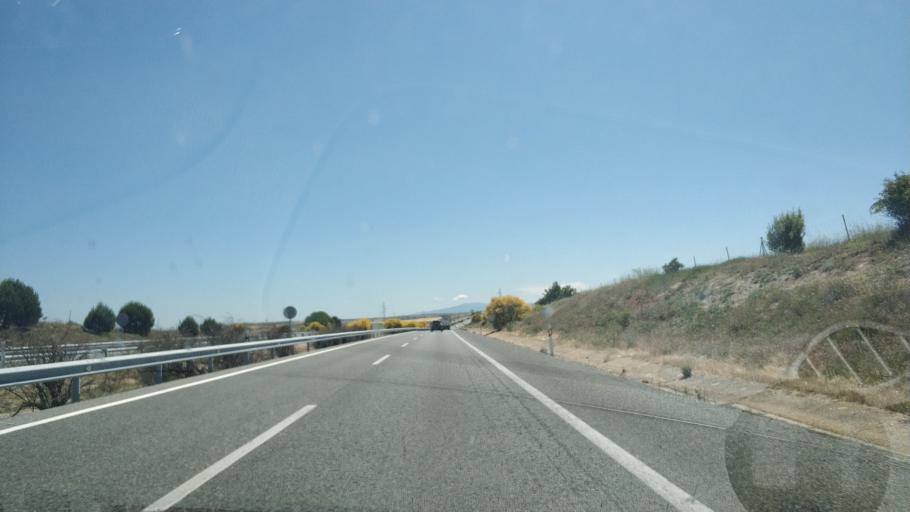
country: ES
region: Castille and Leon
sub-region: Provincia de Burgos
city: Buniel
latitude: 42.3071
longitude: -3.7970
